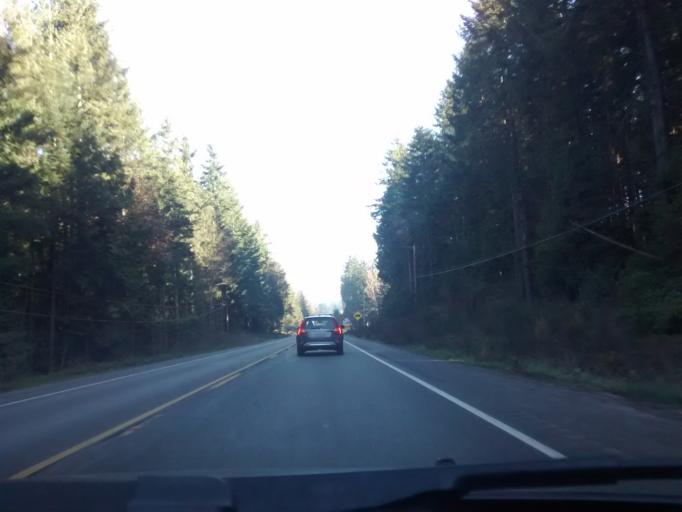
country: US
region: Washington
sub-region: Kitsap County
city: Lofall
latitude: 47.8078
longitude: -122.6476
